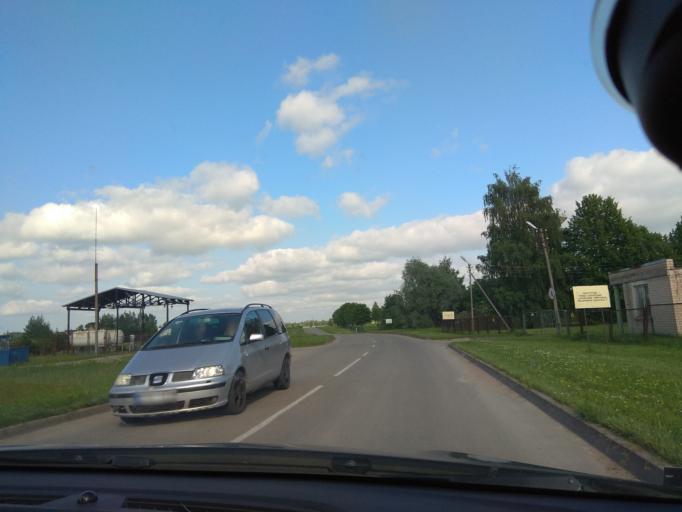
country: LT
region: Siauliu apskritis
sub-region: Joniskis
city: Joniskis
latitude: 56.2281
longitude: 23.6128
